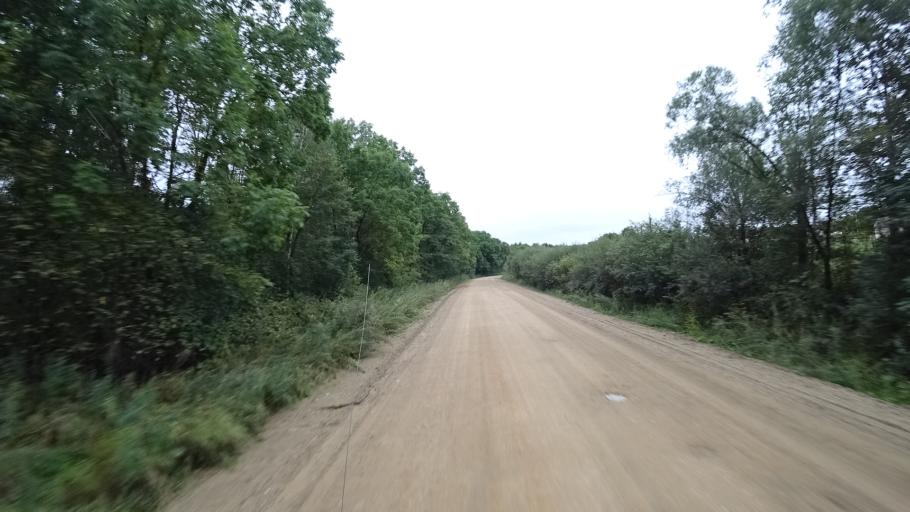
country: RU
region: Primorskiy
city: Rettikhovka
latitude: 44.1798
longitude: 132.8518
